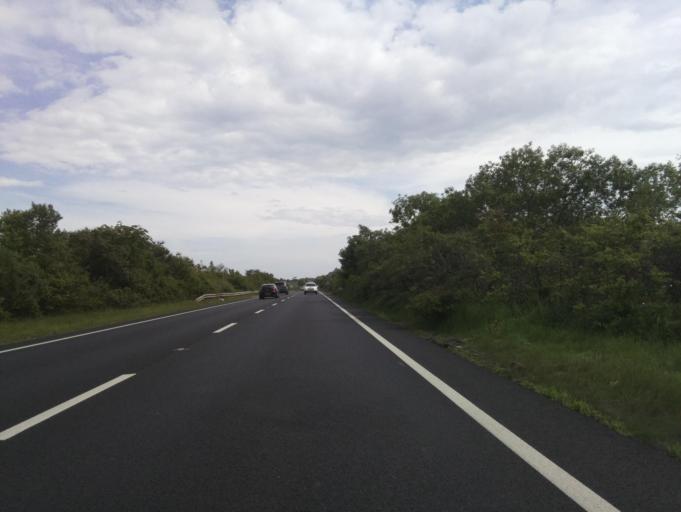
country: GB
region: England
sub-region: Northumberland
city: Belford
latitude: 55.6155
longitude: -1.8342
